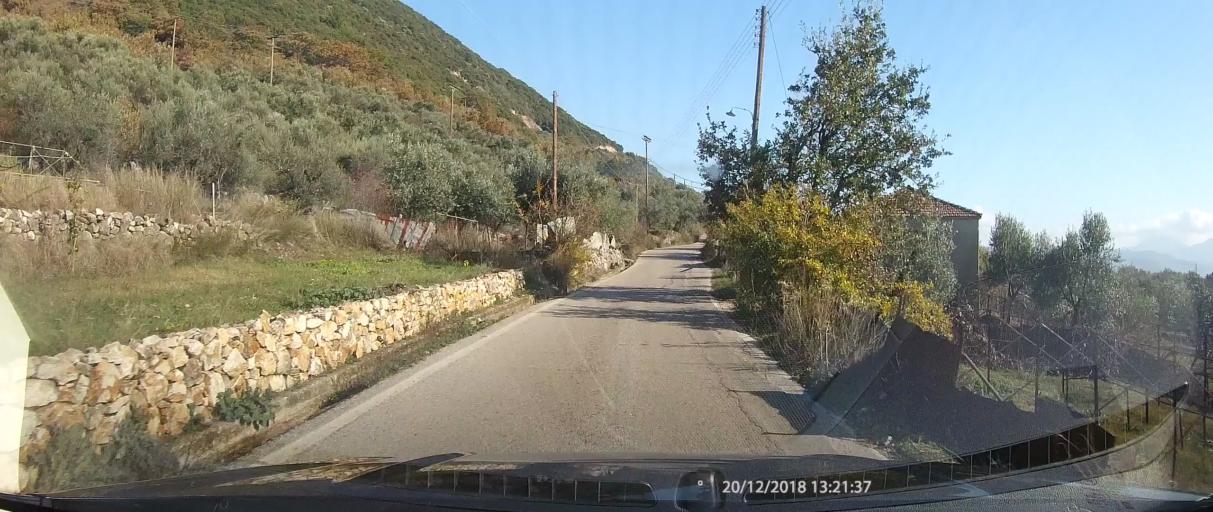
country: GR
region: West Greece
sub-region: Nomos Aitolias kai Akarnanias
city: Paravola
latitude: 38.6167
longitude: 21.5575
